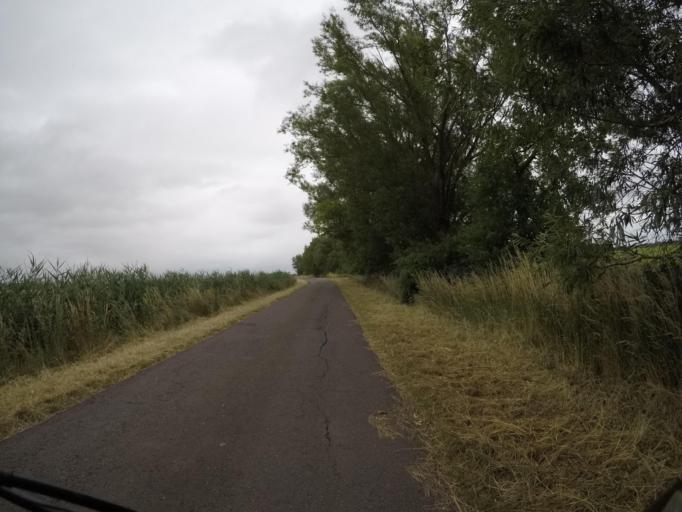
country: DE
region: Lower Saxony
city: Hitzacker
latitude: 53.1749
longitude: 11.0854
